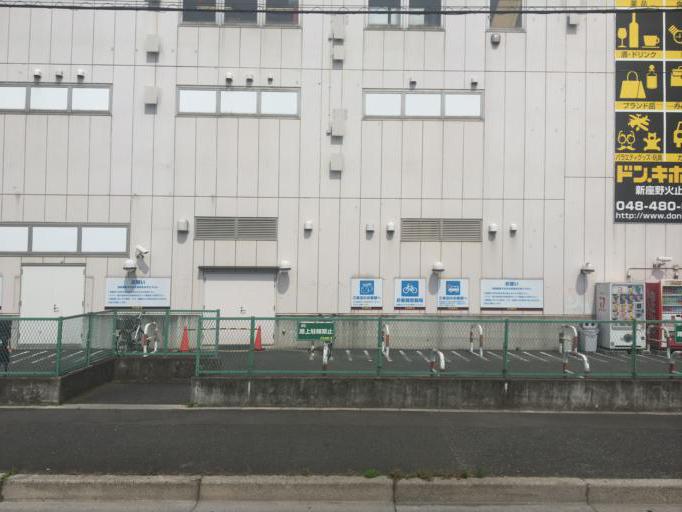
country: JP
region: Saitama
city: Asaka
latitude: 35.7972
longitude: 139.5669
